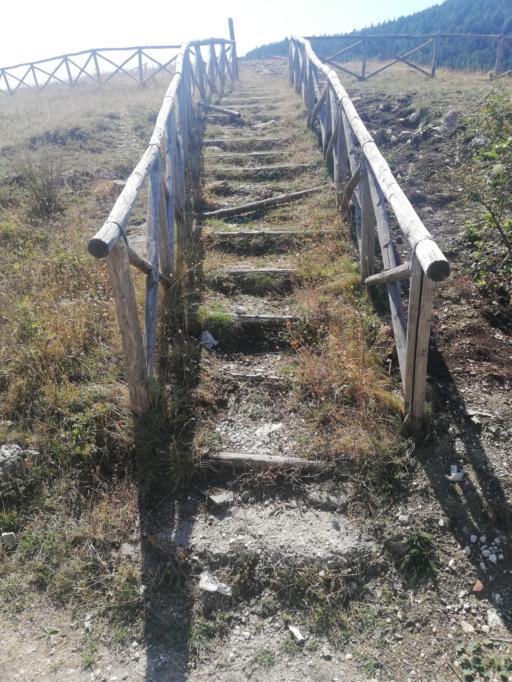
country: IT
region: Apulia
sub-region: Provincia di Foggia
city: Biccari
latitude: 41.3700
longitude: 15.1719
